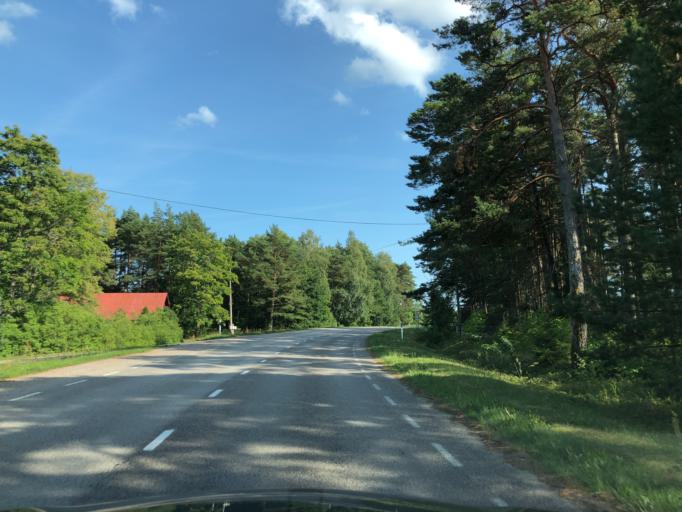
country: EE
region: Hiiumaa
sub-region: Kaerdla linn
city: Kardla
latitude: 58.7071
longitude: 22.5939
